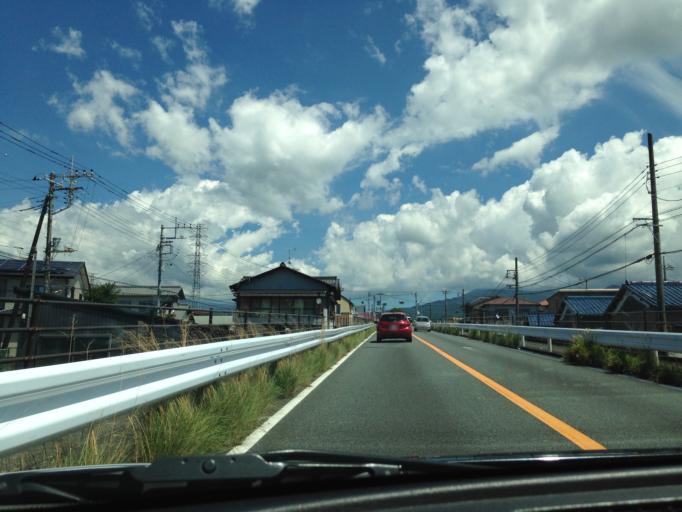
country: JP
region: Shizuoka
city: Fuji
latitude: 35.1758
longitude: 138.6935
